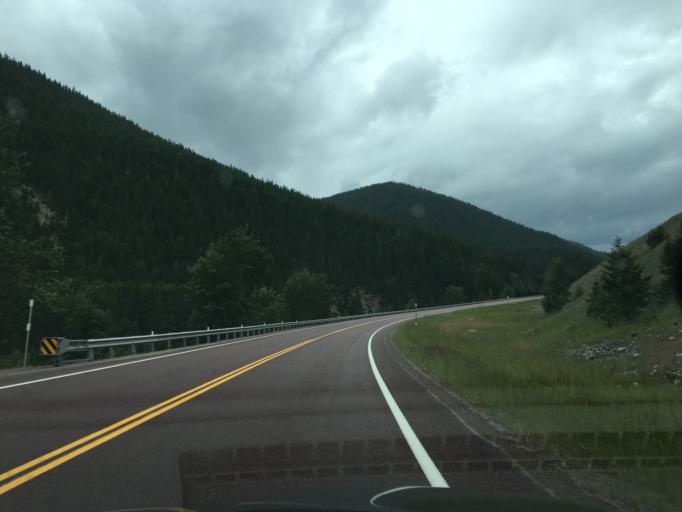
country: US
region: Montana
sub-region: Flathead County
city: Bigfork
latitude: 48.2346
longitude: -113.5663
